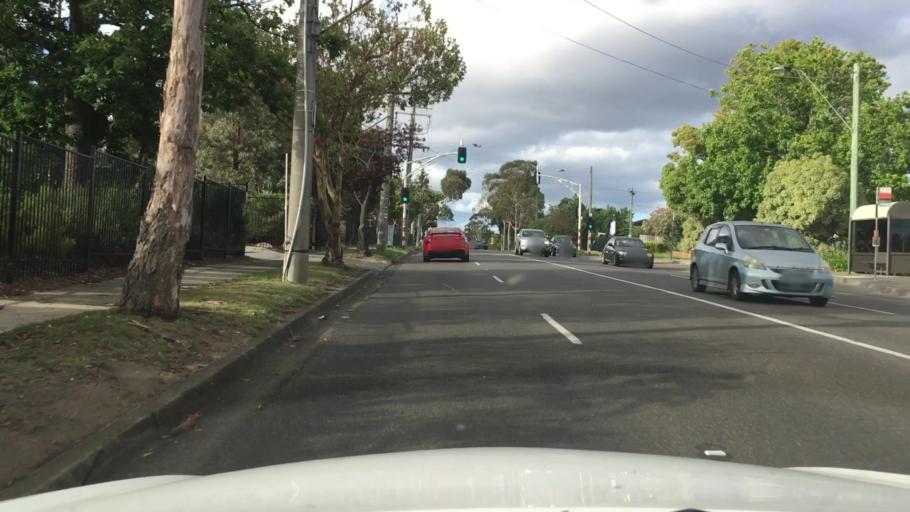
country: AU
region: Victoria
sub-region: Whitehorse
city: Burwood
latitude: -37.8660
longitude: 145.1308
